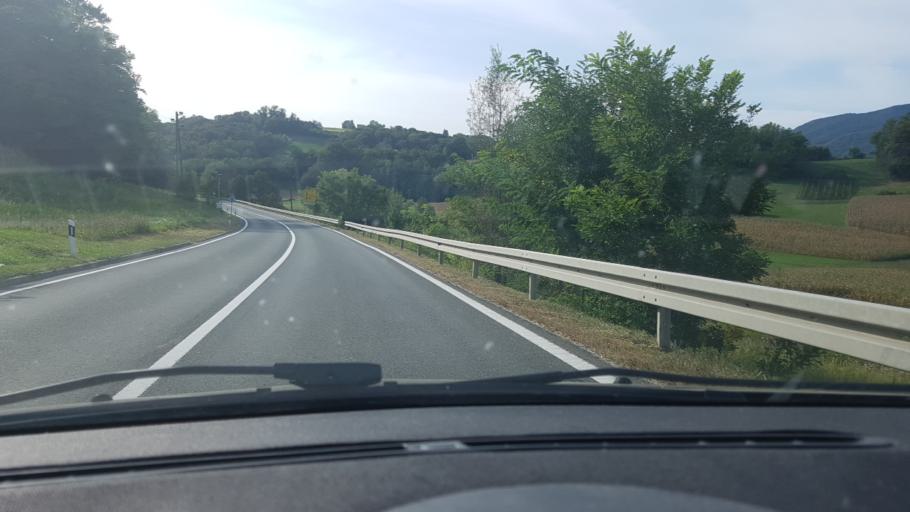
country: HR
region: Krapinsko-Zagorska
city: Radoboj
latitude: 46.1491
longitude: 15.9475
